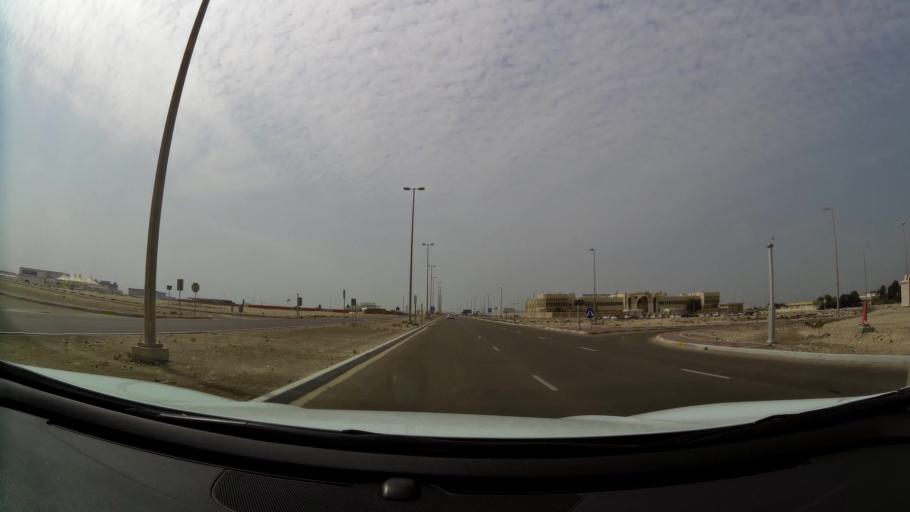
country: AE
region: Abu Dhabi
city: Abu Dhabi
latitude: 24.5404
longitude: 54.6803
